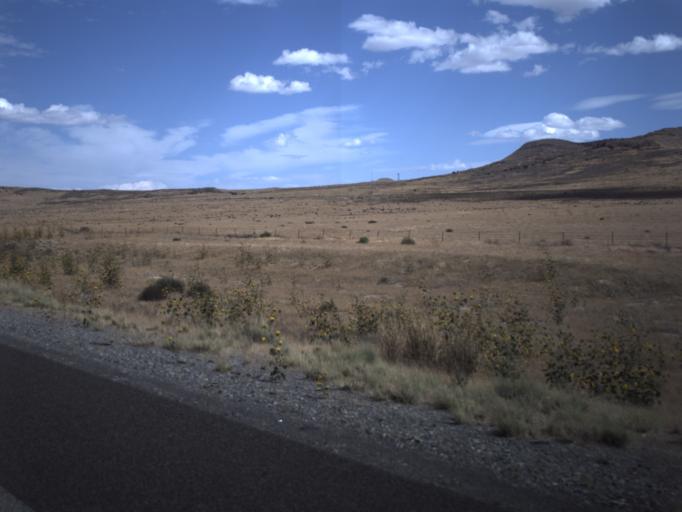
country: US
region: Utah
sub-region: Tooele County
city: Grantsville
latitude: 40.7956
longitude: -112.9486
